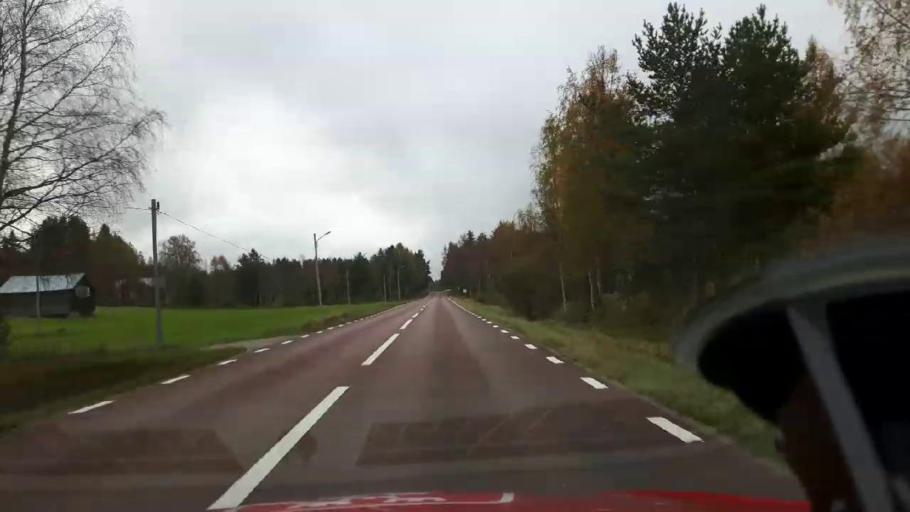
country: SE
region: Jaemtland
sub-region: Harjedalens Kommun
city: Sveg
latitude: 62.3079
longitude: 14.7645
